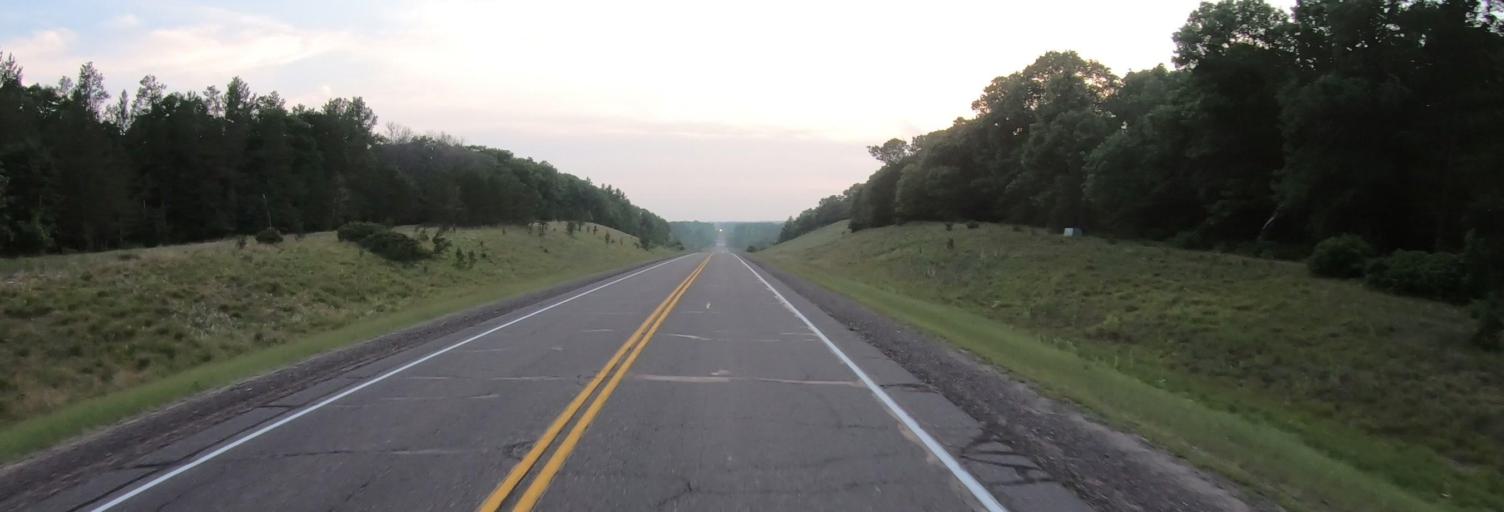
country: US
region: Wisconsin
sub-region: Burnett County
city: Grantsburg
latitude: 45.7731
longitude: -92.7673
